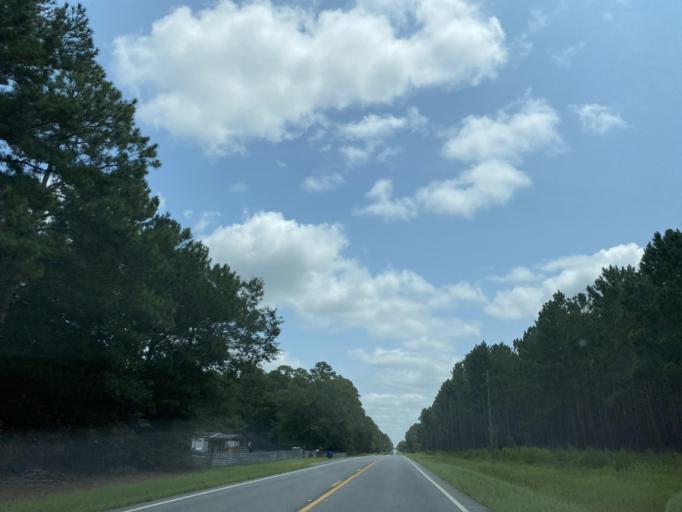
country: US
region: Georgia
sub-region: Bacon County
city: Alma
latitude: 31.6984
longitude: -82.5103
